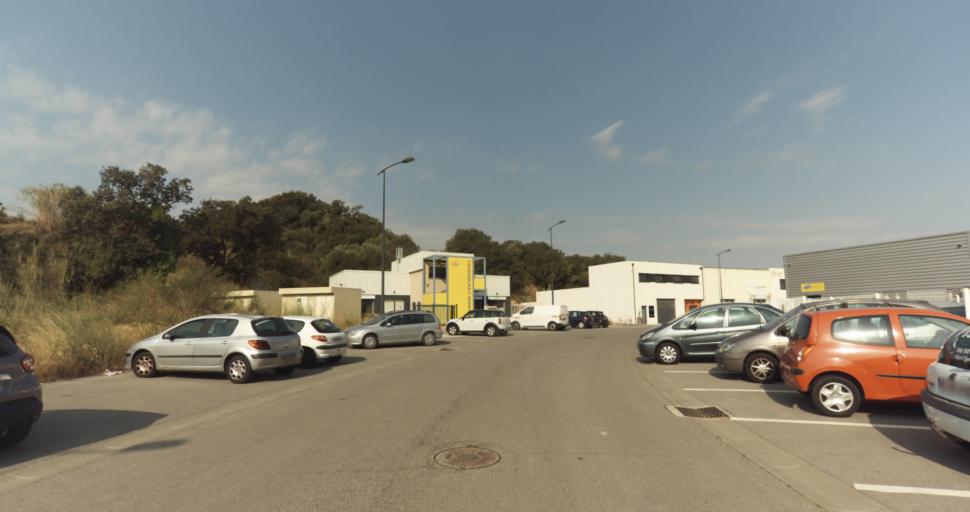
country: FR
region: Languedoc-Roussillon
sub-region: Departement des Pyrenees-Orientales
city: Latour-Bas-Elne
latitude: 42.6132
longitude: 2.9933
